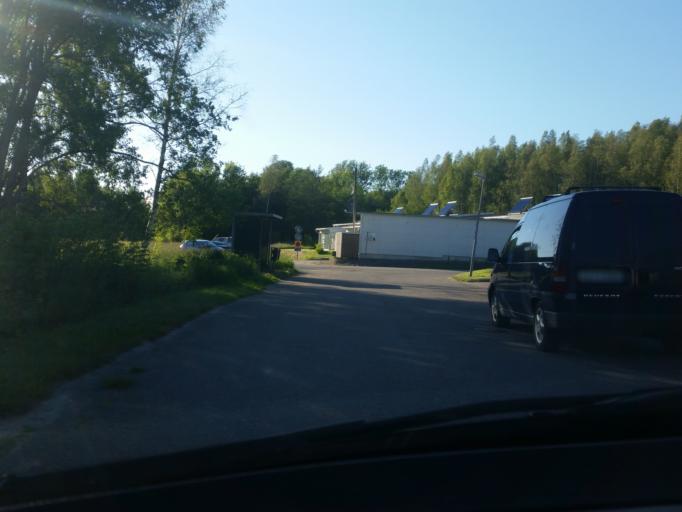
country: SE
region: Vaestra Goetaland
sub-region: Fargelanda Kommun
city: Faergelanda
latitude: 58.5157
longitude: 11.9784
